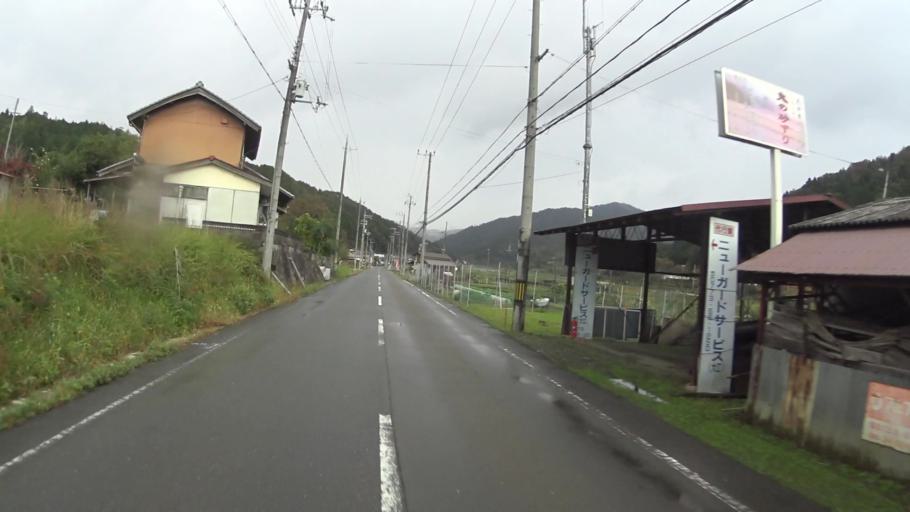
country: JP
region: Kyoto
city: Fukuchiyama
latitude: 35.4110
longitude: 135.1519
